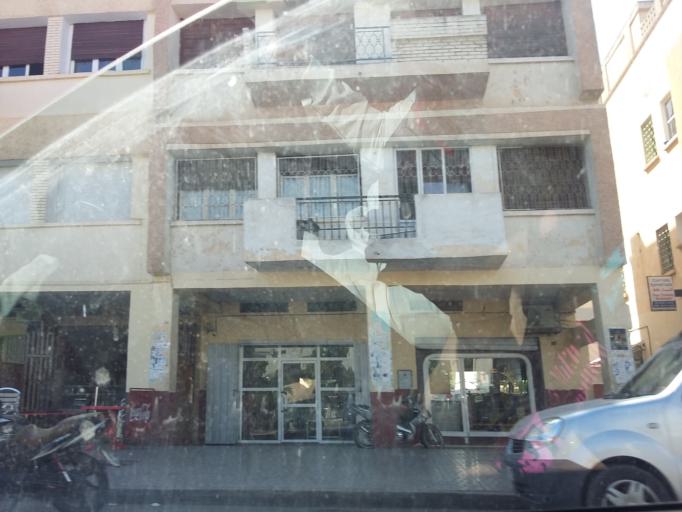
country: MA
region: Fes-Boulemane
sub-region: Fes
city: Fes
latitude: 34.0244
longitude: -5.0054
